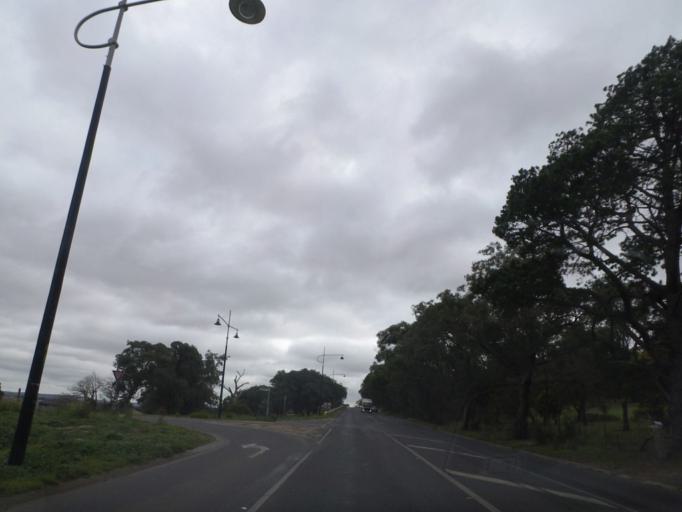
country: AU
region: Victoria
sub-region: Nillumbik
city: Doreen
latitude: -37.6201
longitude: 145.1357
